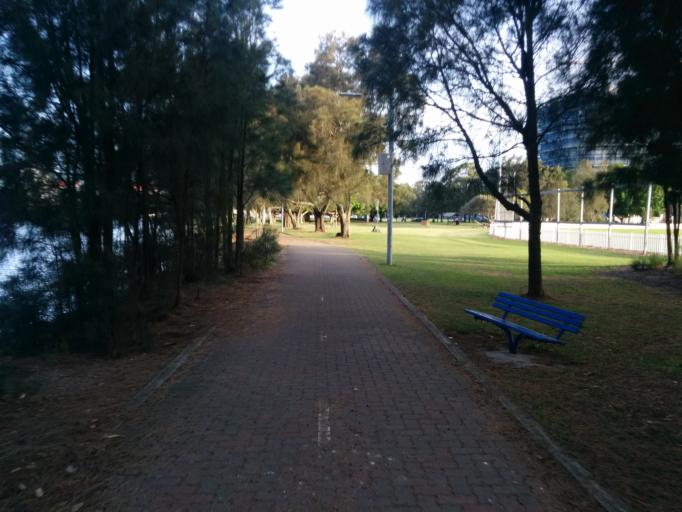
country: AU
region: New South Wales
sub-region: Rockdale
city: Arncliffe
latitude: -33.9320
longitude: 151.1562
